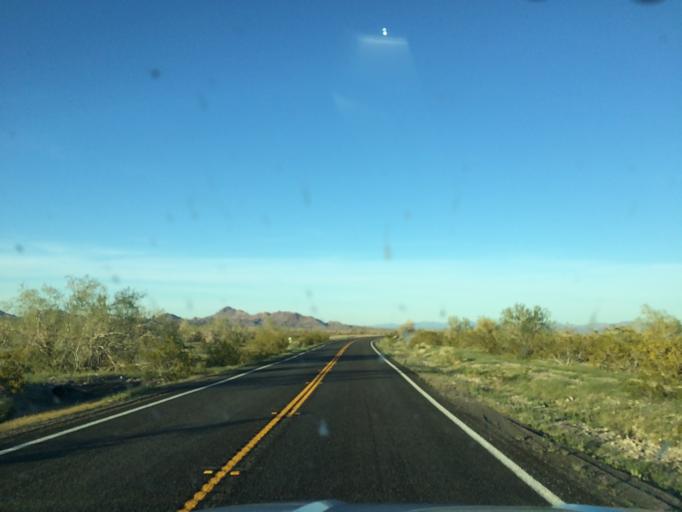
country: US
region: California
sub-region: Riverside County
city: Mesa Verde
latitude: 33.2419
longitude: -114.8314
